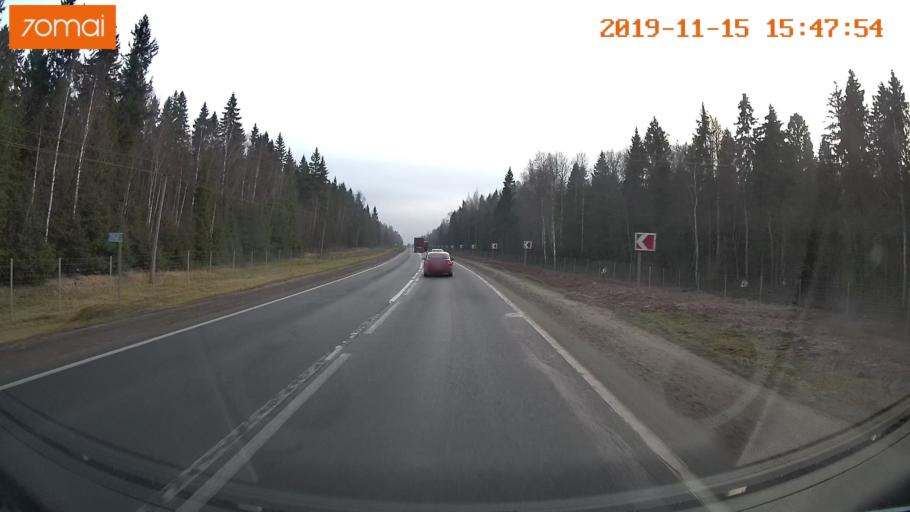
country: RU
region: Jaroslavl
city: Danilov
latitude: 57.9333
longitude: 40.0065
